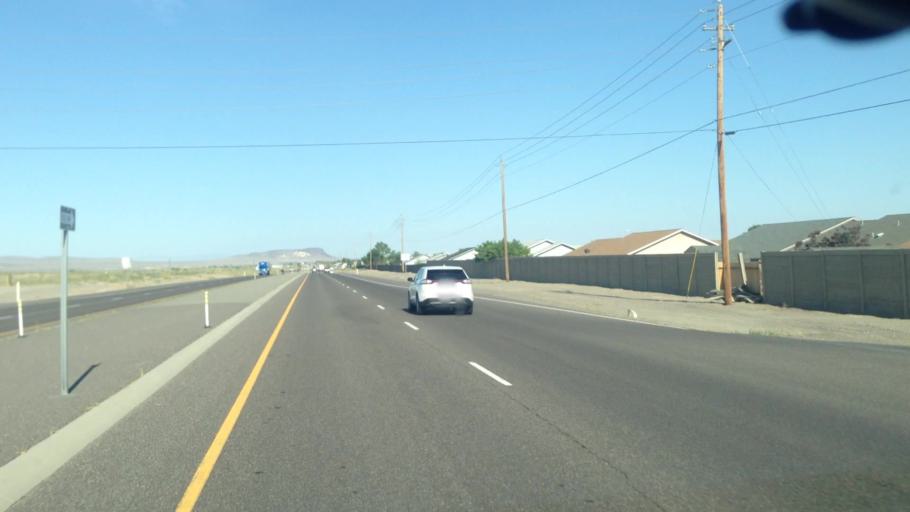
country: US
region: Nevada
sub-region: Lyon County
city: Fernley
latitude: 39.5996
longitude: -119.2069
